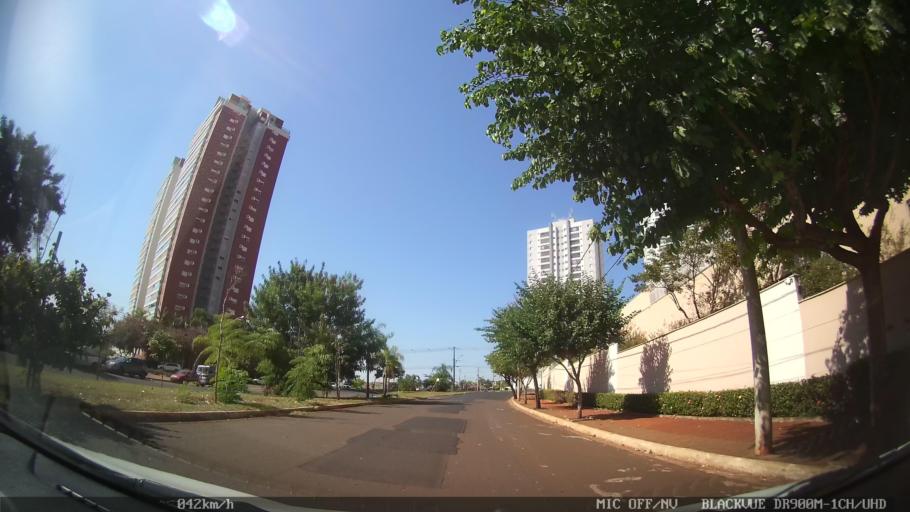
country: BR
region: Sao Paulo
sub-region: Ribeirao Preto
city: Ribeirao Preto
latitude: -21.2194
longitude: -47.7966
